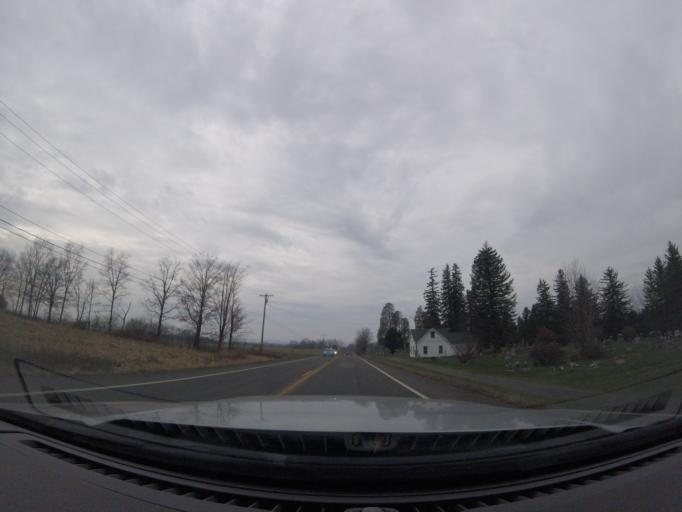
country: US
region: New York
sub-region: Schuyler County
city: Watkins Glen
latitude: 42.4239
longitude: -76.8219
